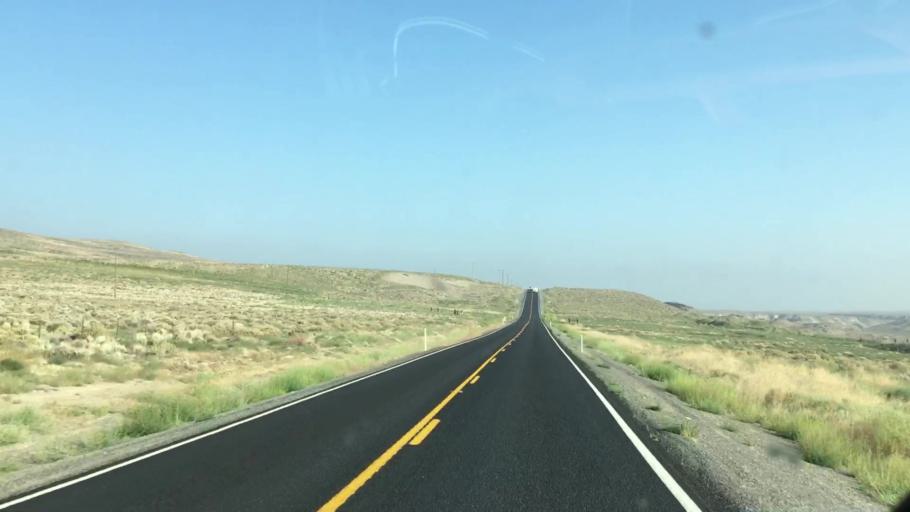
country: US
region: Nevada
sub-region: Lyon County
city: Fernley
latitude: 39.7587
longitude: -119.3381
